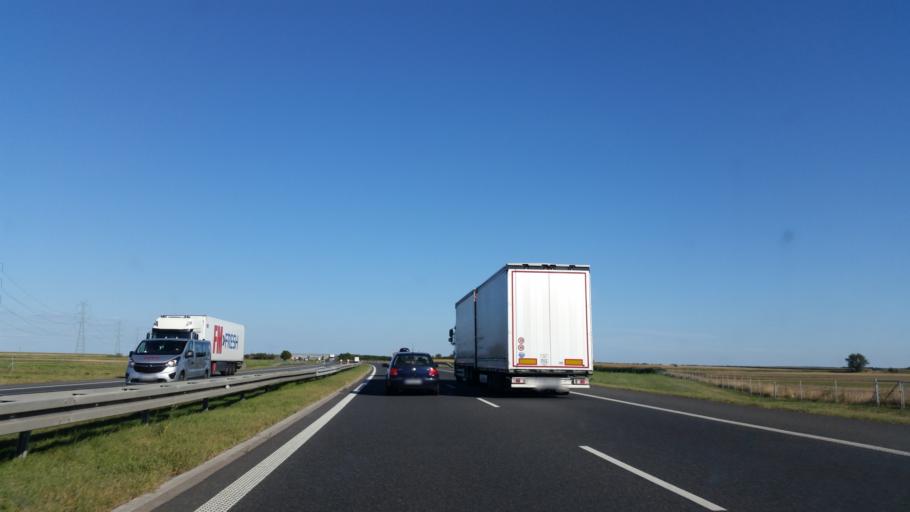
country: PL
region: Opole Voivodeship
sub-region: Powiat brzeski
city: Olszanka
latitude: 50.7412
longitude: 17.4606
